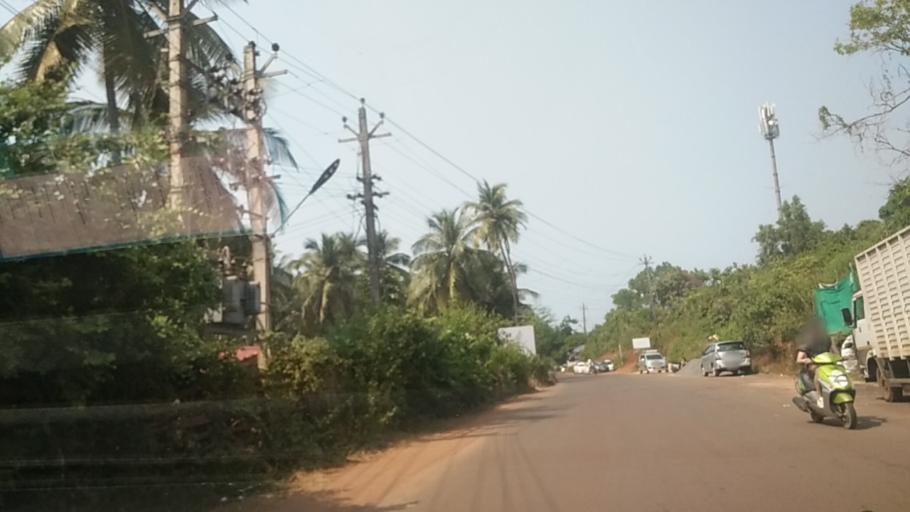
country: IN
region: Goa
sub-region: North Goa
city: Arambol
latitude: 15.6706
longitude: 73.7113
